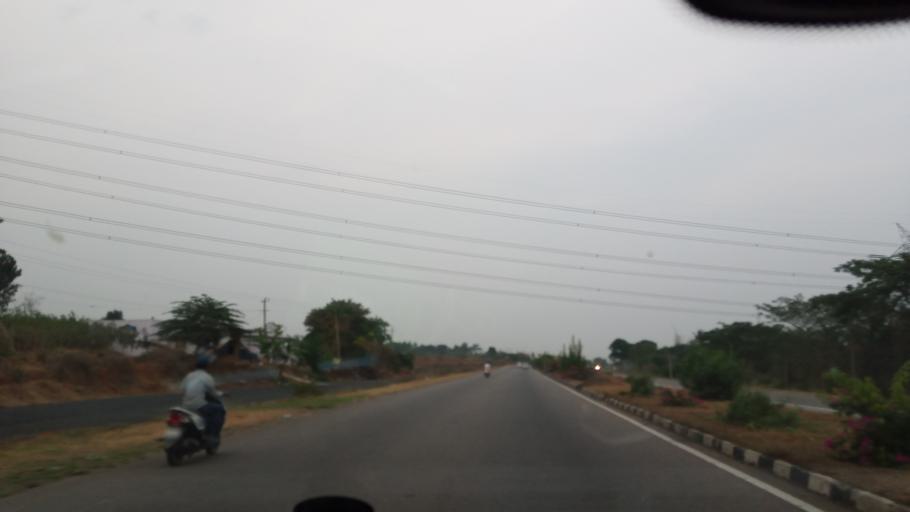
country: IN
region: Karnataka
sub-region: Ramanagara
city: Magadi
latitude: 13.0761
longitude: 77.2018
